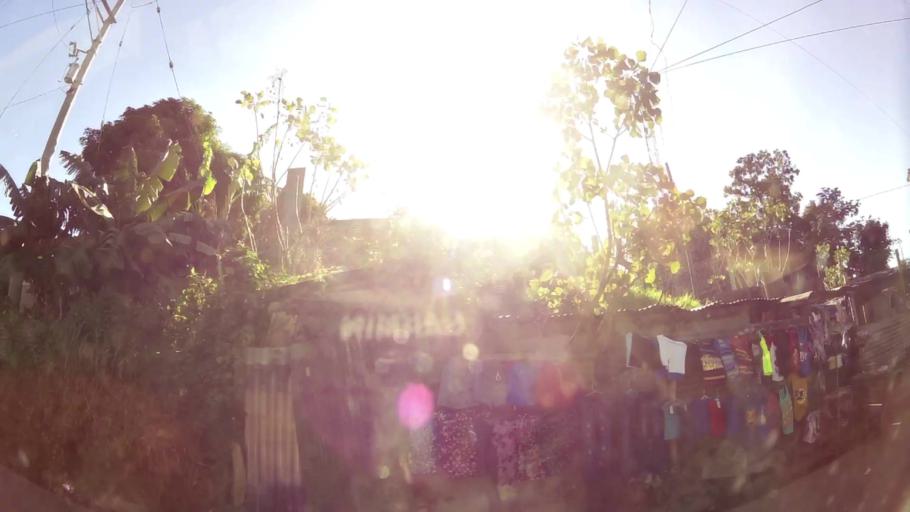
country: SV
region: Sonsonate
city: Sonzacate
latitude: 13.7382
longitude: -89.7146
